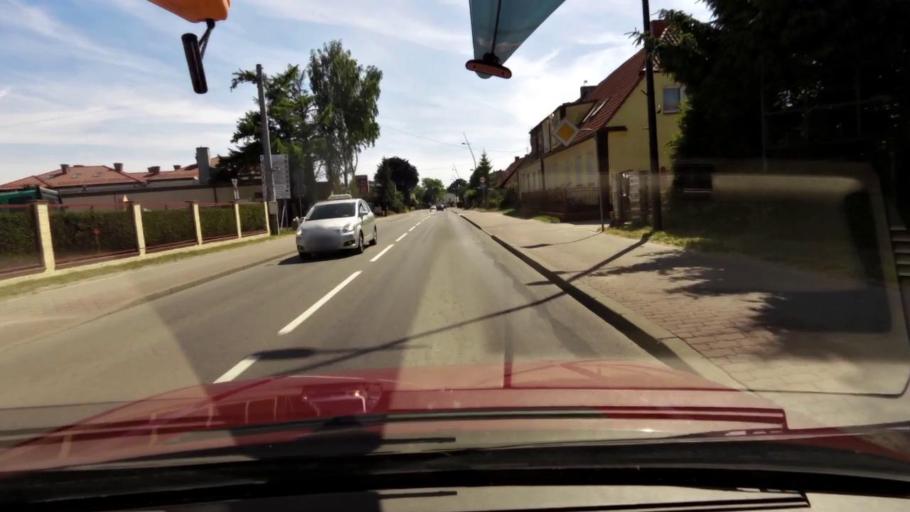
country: PL
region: Pomeranian Voivodeship
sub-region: Powiat slupski
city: Kobylnica
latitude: 54.4425
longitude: 16.9996
